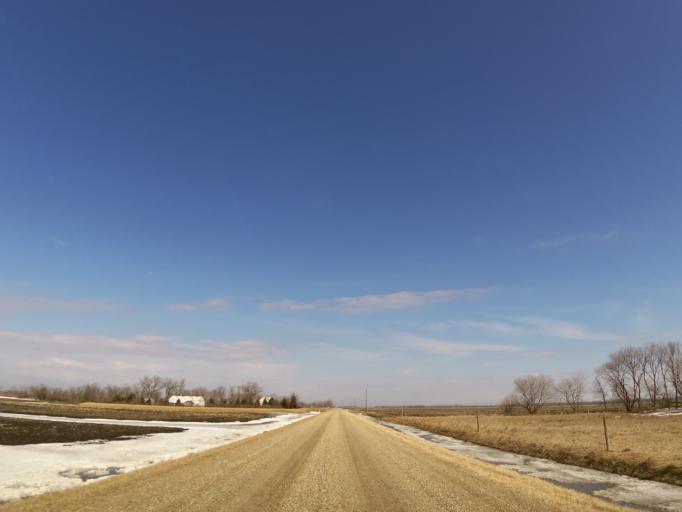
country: US
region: North Dakota
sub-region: Walsh County
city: Grafton
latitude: 48.3924
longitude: -97.1684
